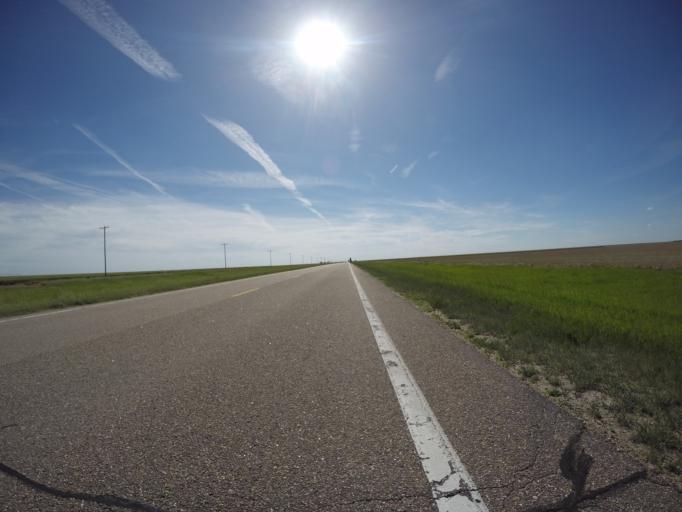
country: US
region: Kansas
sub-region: Cheyenne County
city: Saint Francis
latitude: 39.7567
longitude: -101.9597
